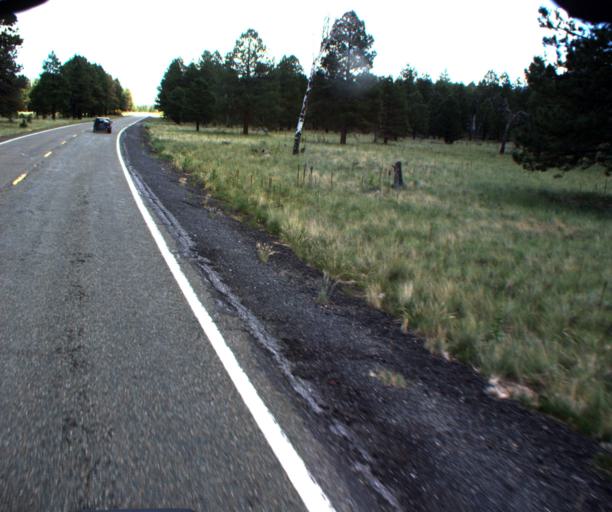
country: US
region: Arizona
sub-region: Coconino County
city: Parks
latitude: 35.3961
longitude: -111.7665
